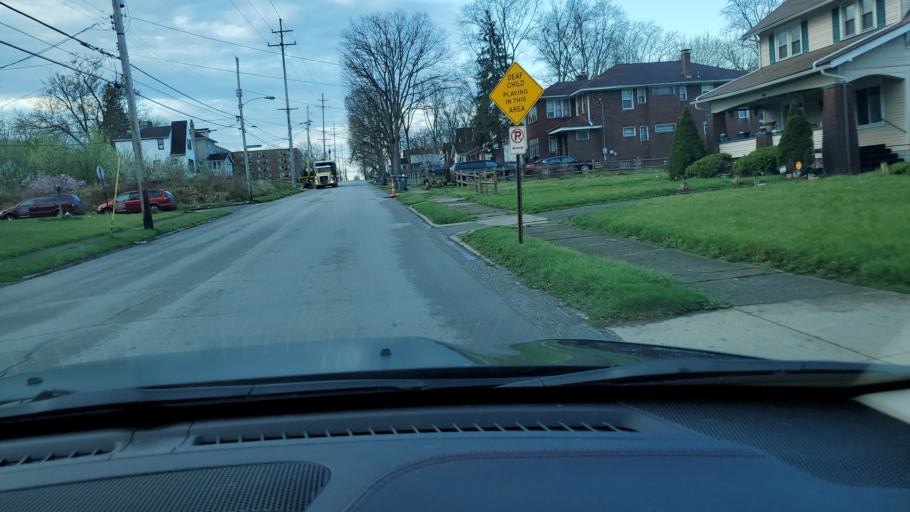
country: US
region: Ohio
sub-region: Mahoning County
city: Youngstown
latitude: 41.0659
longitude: -80.6640
